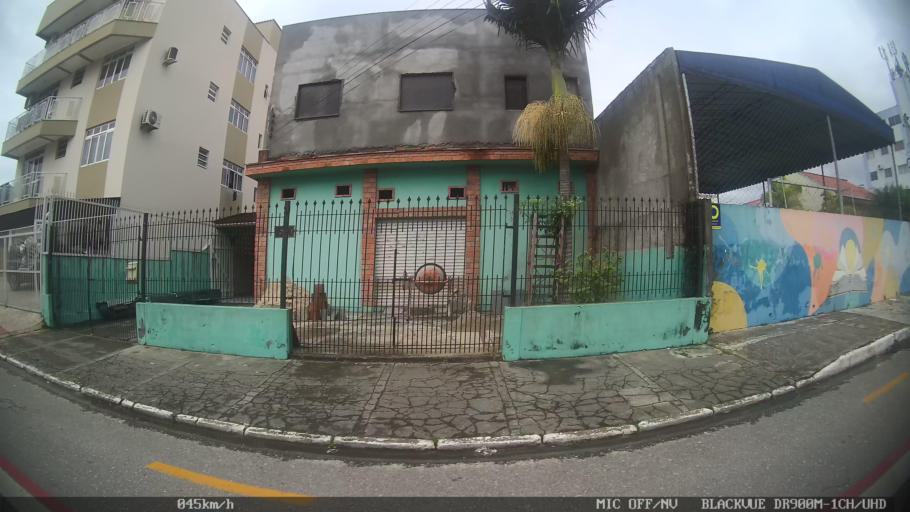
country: BR
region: Santa Catarina
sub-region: Sao Jose
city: Campinas
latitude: -27.5585
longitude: -48.6298
